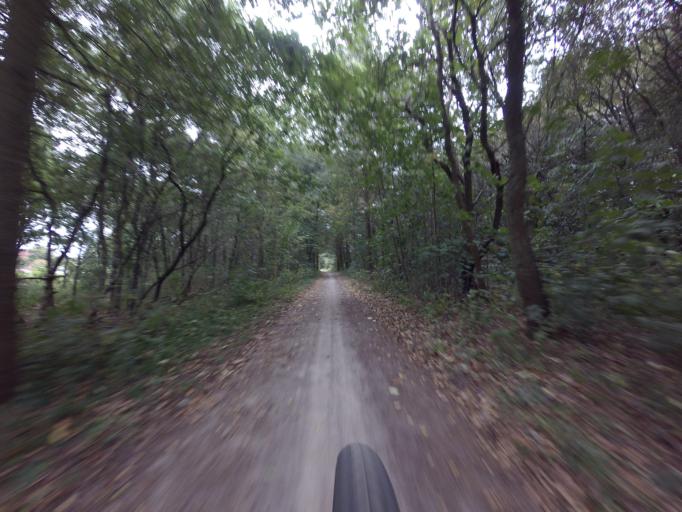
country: DK
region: South Denmark
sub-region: Billund Kommune
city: Grindsted
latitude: 55.7707
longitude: 8.9261
